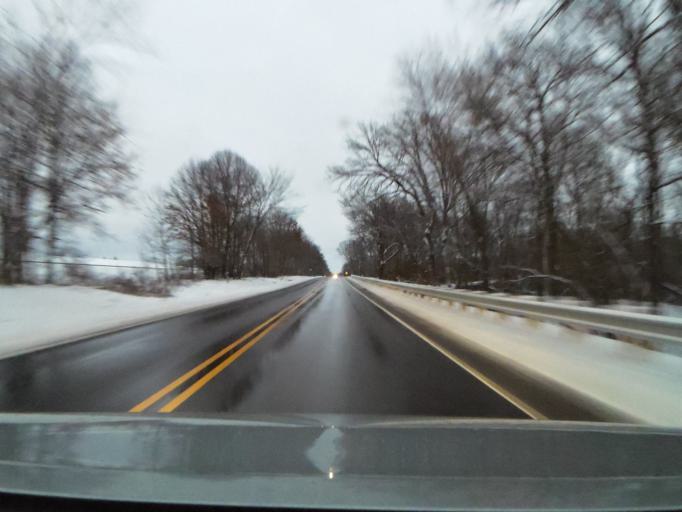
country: US
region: Wisconsin
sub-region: Dunn County
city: Boyceville
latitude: 44.9408
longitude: -92.0298
